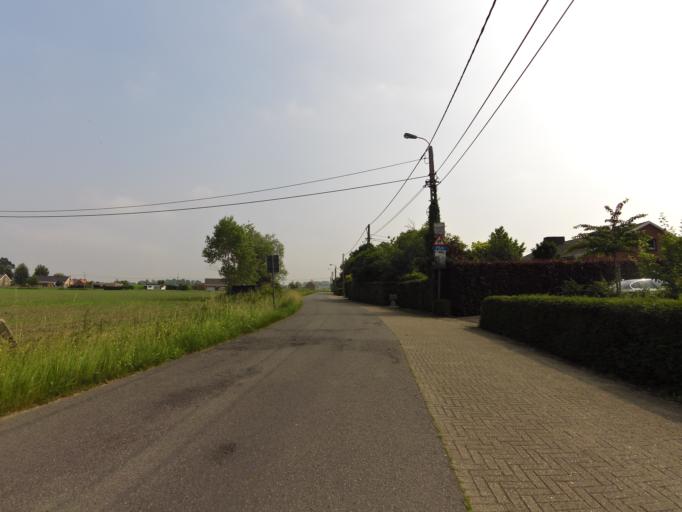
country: BE
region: Flanders
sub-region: Provincie West-Vlaanderen
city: Ichtegem
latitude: 51.1173
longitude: 3.0665
